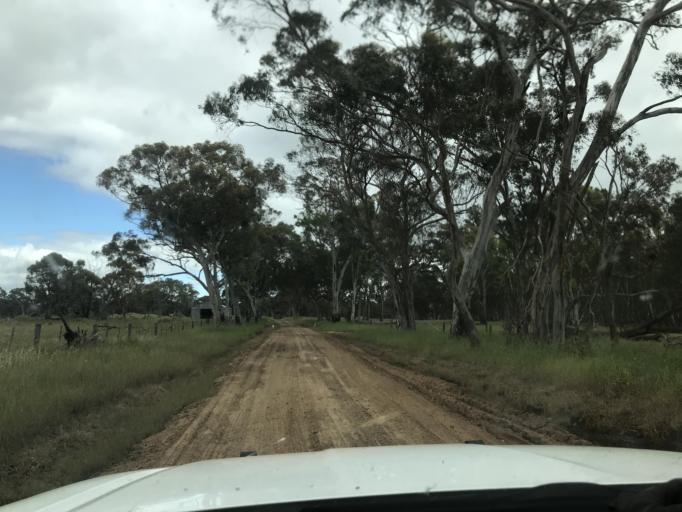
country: AU
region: South Australia
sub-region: Wattle Range
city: Penola
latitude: -37.1222
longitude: 141.2224
